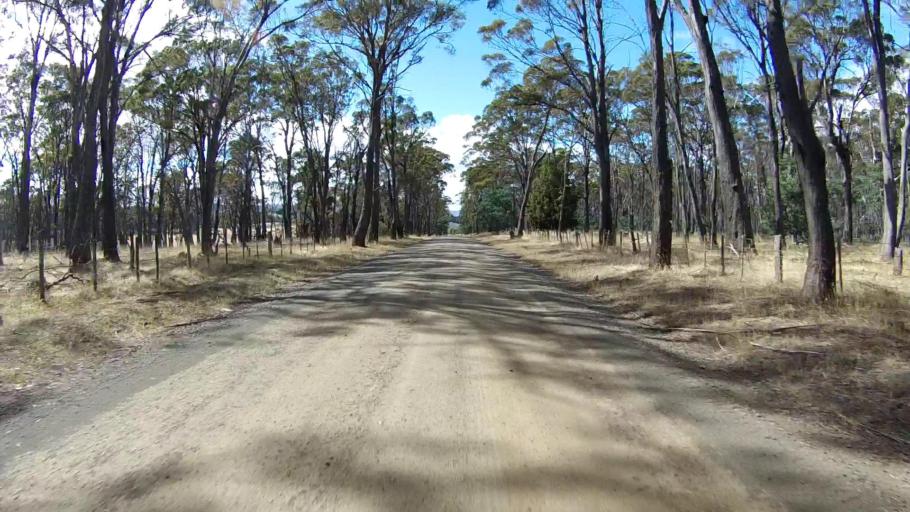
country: AU
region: Tasmania
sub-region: Northern Midlands
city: Evandale
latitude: -41.7291
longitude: 147.4439
